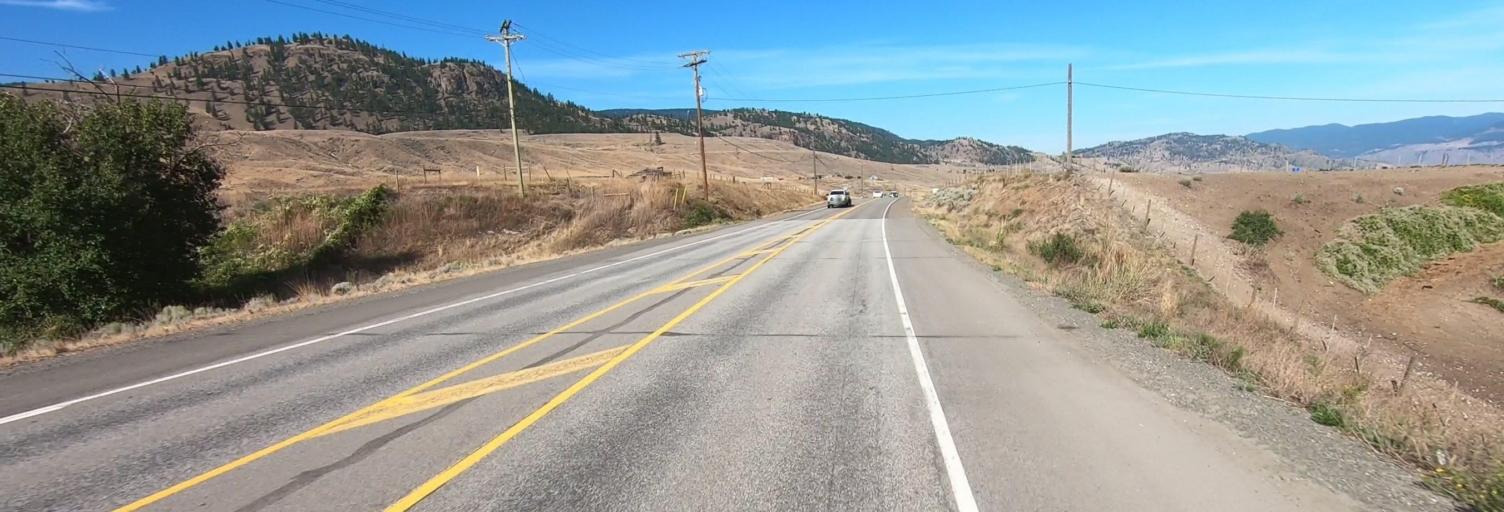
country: CA
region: British Columbia
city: Logan Lake
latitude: 50.7176
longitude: -120.6416
